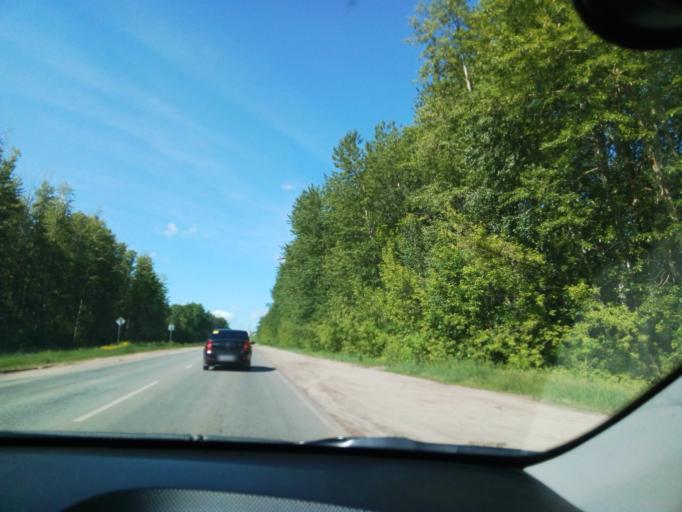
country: RU
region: Chuvashia
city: Novocheboksarsk
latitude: 56.0807
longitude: 47.5043
